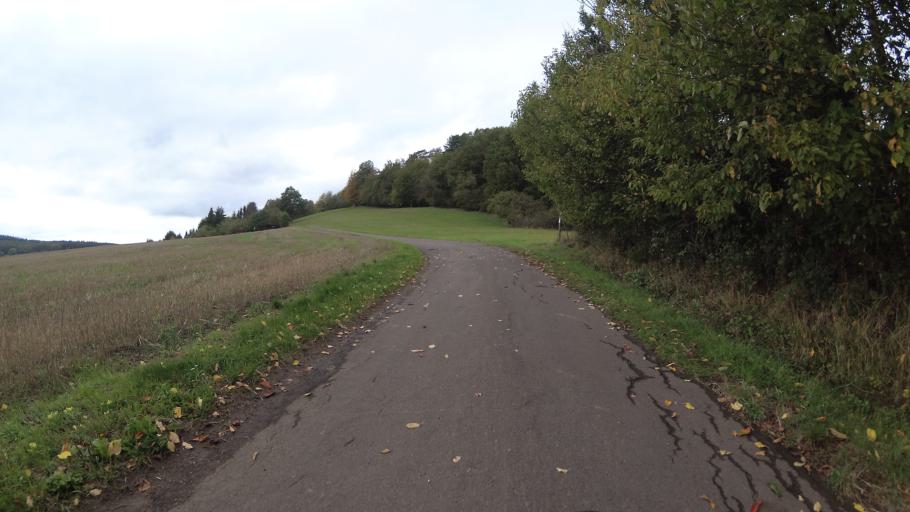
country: DE
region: Rheinland-Pfalz
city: Breitenbach
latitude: 49.4570
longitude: 7.2294
